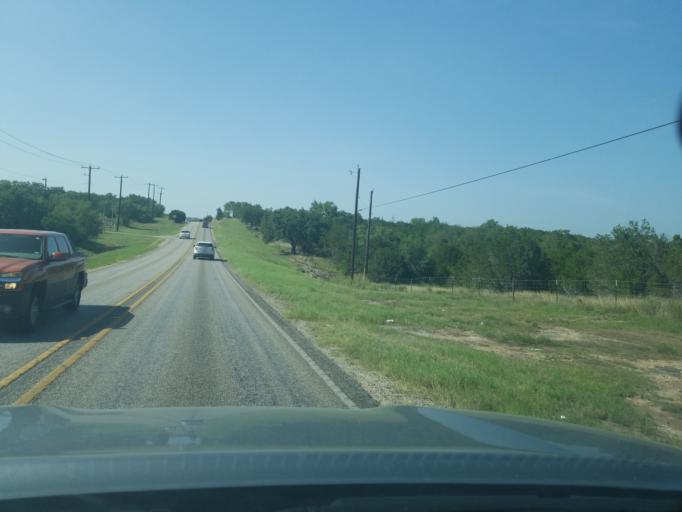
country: US
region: Texas
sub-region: Comal County
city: Garden Ridge
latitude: 29.6722
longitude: -98.3184
